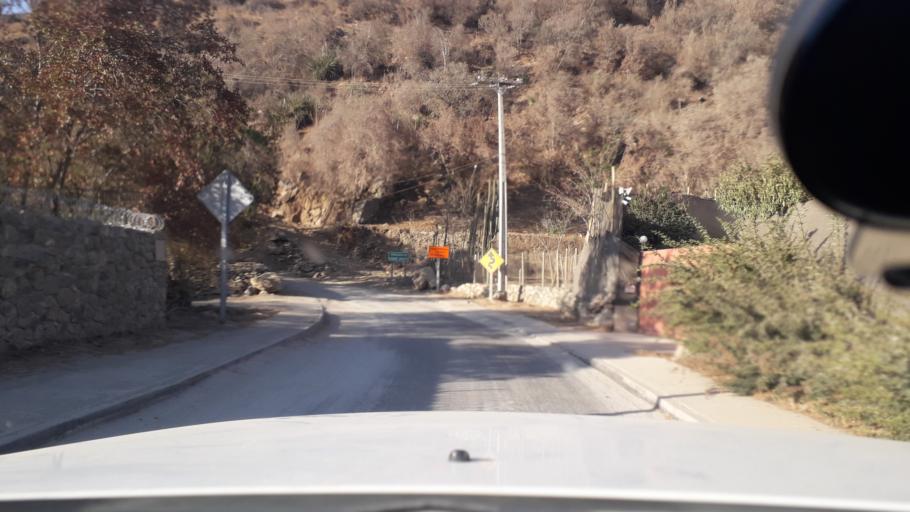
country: CL
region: Valparaiso
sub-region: Provincia de Marga Marga
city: Limache
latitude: -33.0541
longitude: -71.0892
